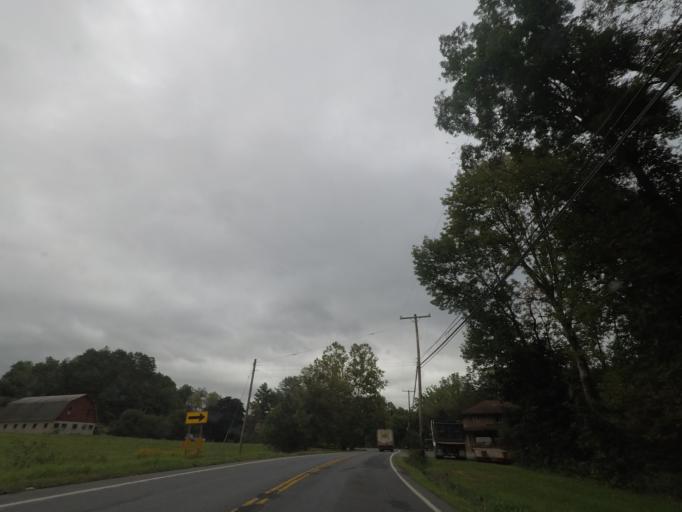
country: US
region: New York
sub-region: Rensselaer County
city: Hoosick Falls
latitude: 42.9310
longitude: -73.3536
